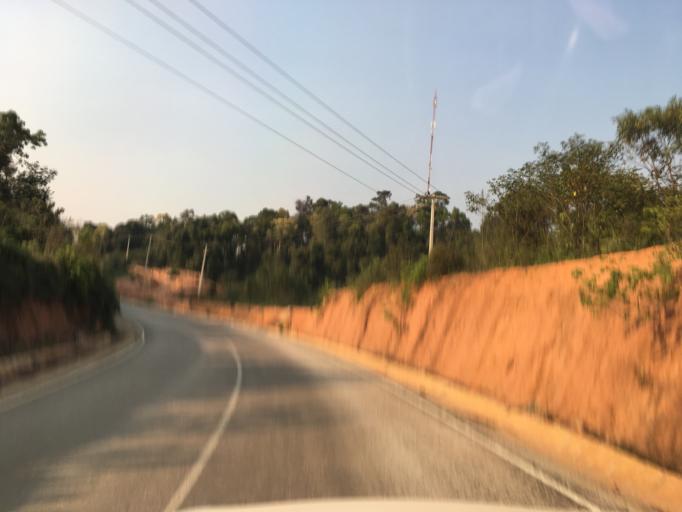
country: LA
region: Houaphan
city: Xam Nua
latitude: 20.6070
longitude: 104.0746
